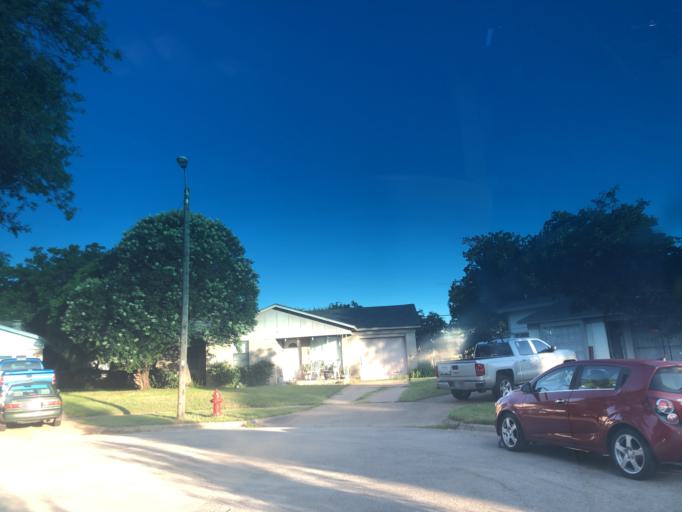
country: US
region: Texas
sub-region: Dallas County
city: Grand Prairie
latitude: 32.7074
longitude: -97.0146
